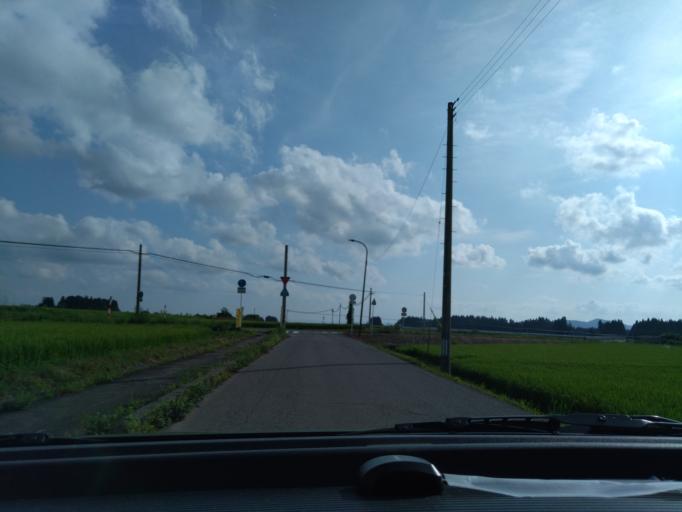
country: JP
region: Akita
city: Kakunodatemachi
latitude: 39.5866
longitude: 140.6062
